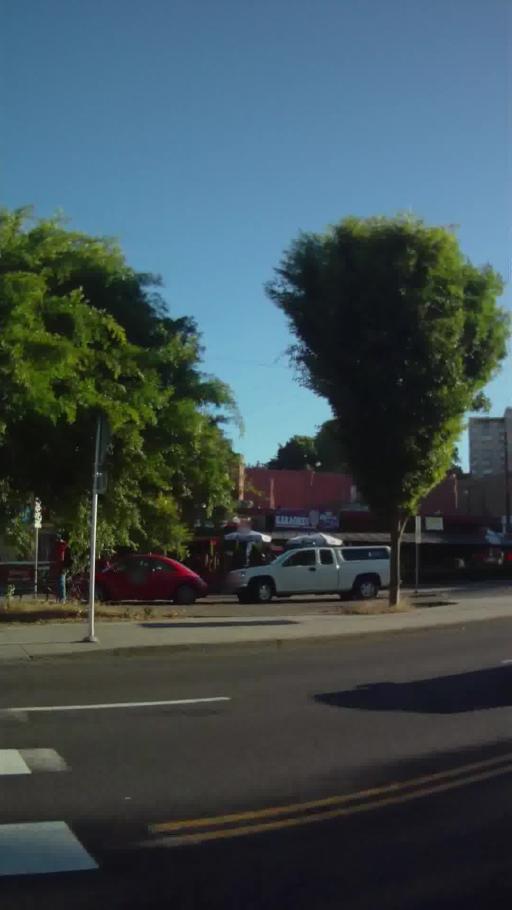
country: US
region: Oregon
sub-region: Multnomah County
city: Portland
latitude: 45.5232
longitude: -122.6935
